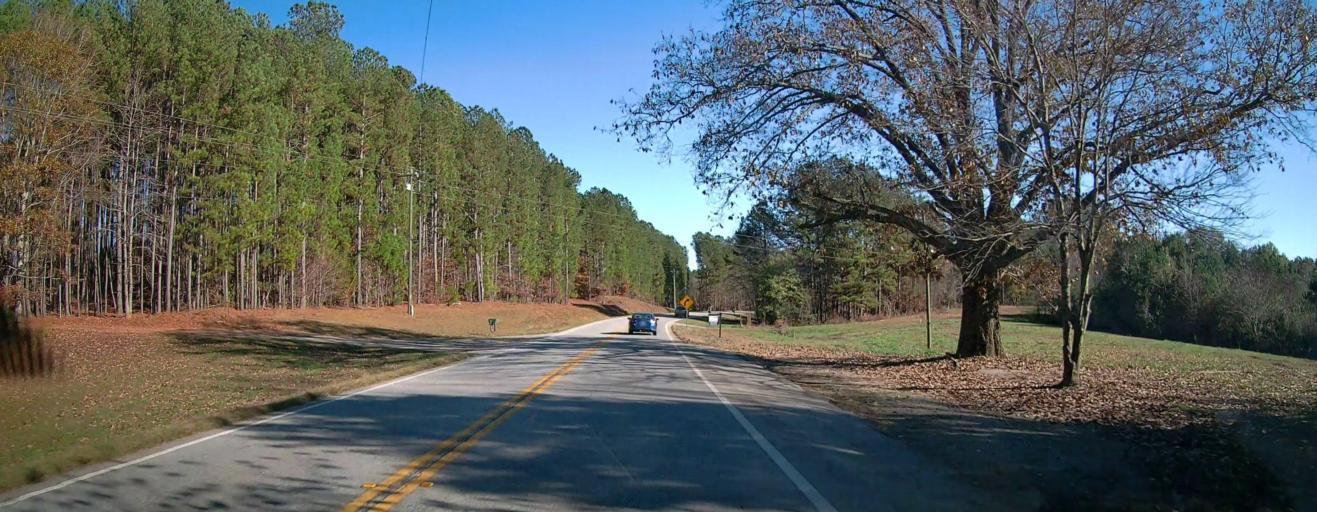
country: US
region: Georgia
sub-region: Hall County
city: Lula
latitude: 34.4426
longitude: -83.7222
